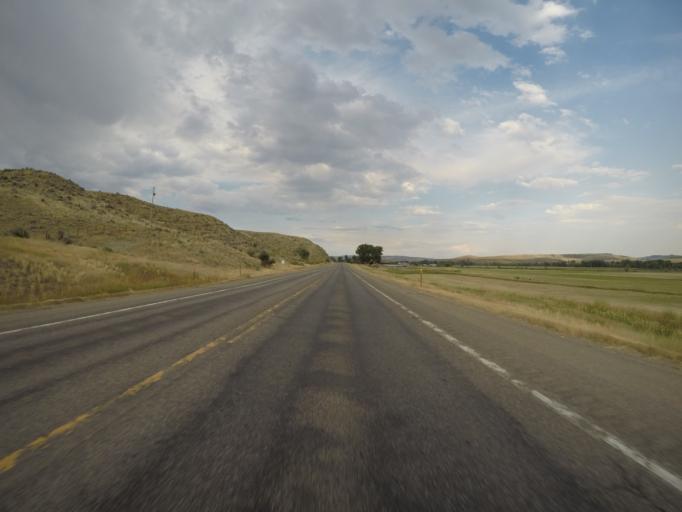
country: US
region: Colorado
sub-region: Moffat County
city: Craig
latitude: 40.5189
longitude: -107.4814
